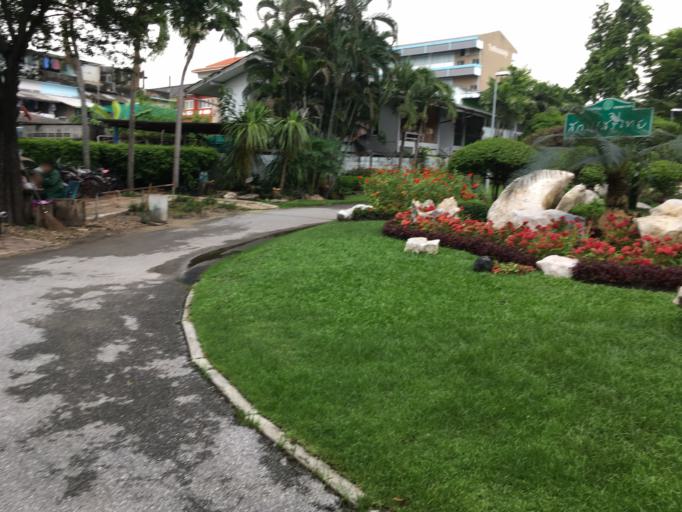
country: TH
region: Bangkok
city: Bueng Kum
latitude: 13.7871
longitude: 100.6744
